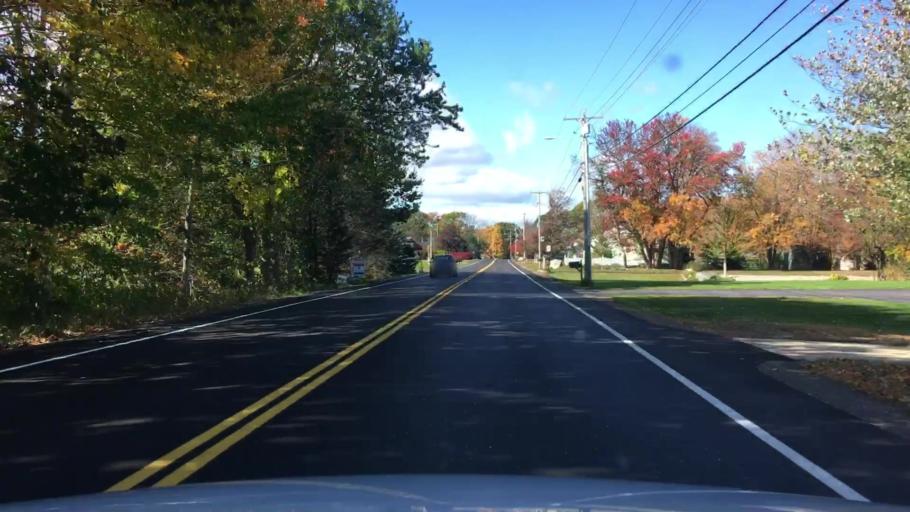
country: US
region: Maine
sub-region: York County
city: Biddeford
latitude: 43.4655
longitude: -70.4419
